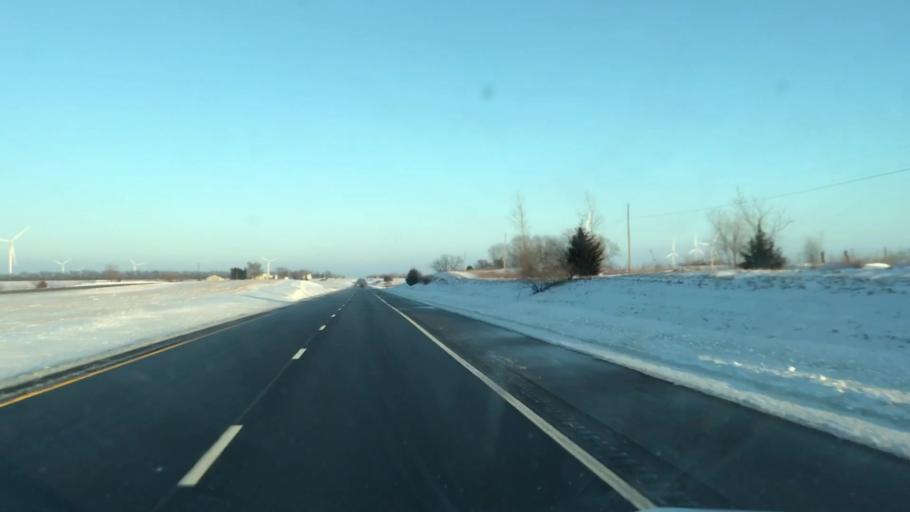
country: US
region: Missouri
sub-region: DeKalb County
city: Maysville
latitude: 39.7616
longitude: -94.4258
